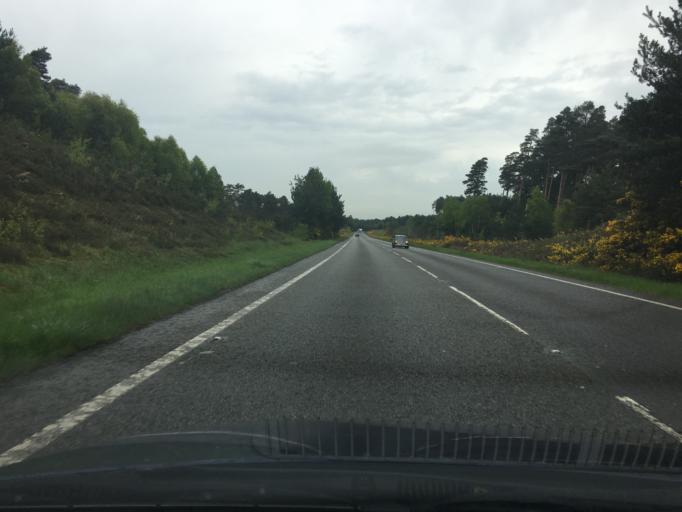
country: GB
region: England
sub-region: Bracknell Forest
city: Crowthorne
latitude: 51.3746
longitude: -0.7672
